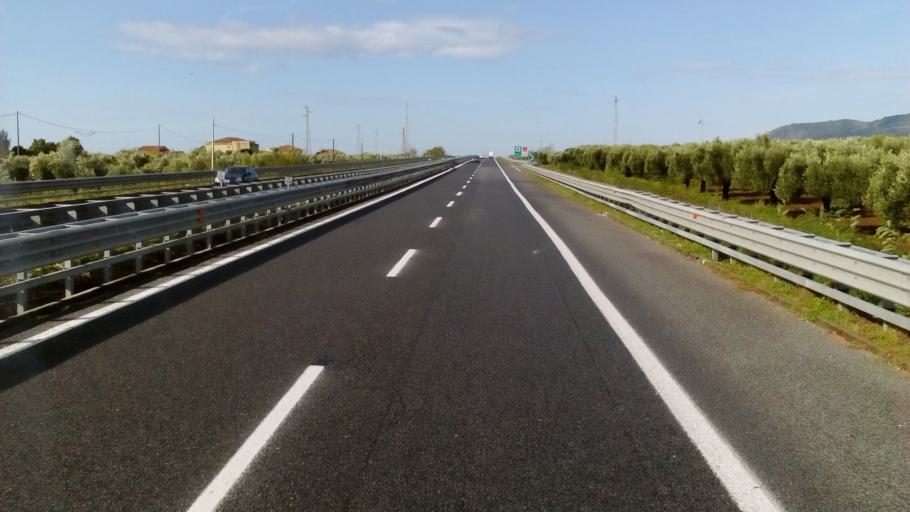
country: IT
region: Calabria
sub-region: Provincia di Catanzaro
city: Santa Eufemia Lamezia
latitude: 38.9243
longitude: 16.2569
